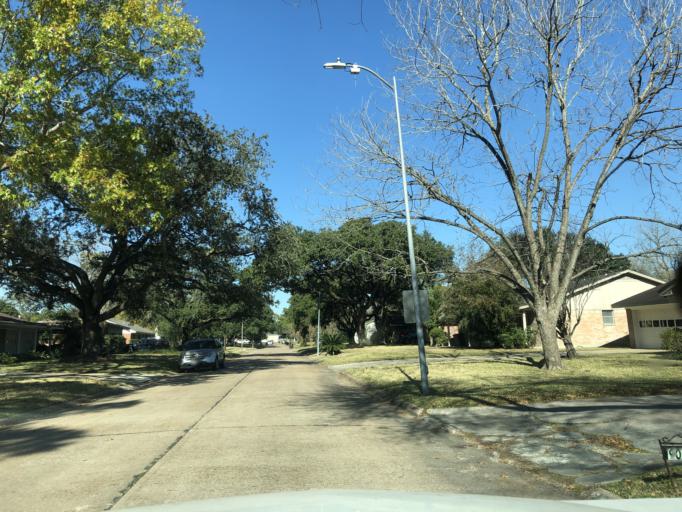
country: US
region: Texas
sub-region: Harris County
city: Bellaire
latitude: 29.6807
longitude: -95.5046
